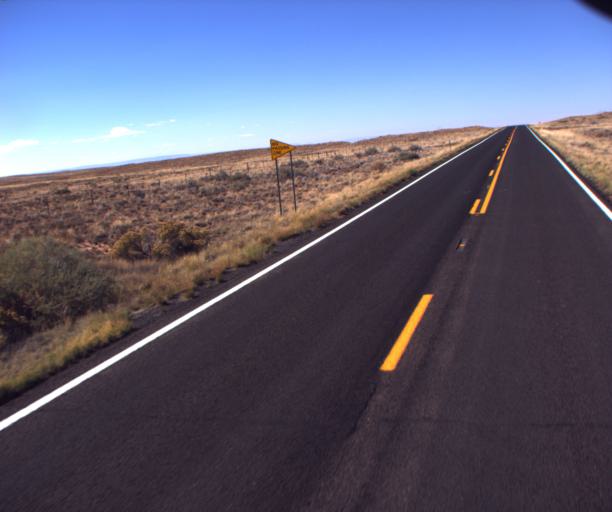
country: US
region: Arizona
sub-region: Coconino County
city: Tuba City
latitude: 35.9686
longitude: -110.9580
